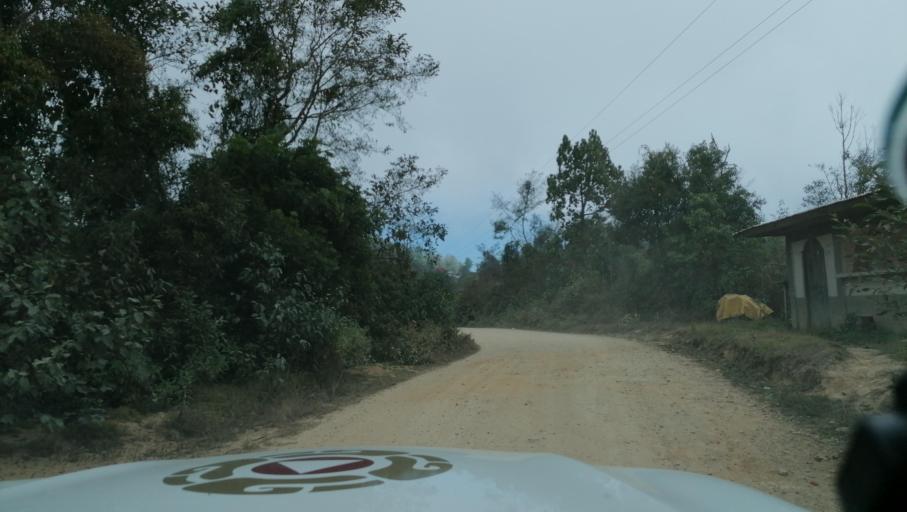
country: MX
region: Chiapas
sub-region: Tapachula
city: Canton Villaflor
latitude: 15.2100
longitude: -92.2404
